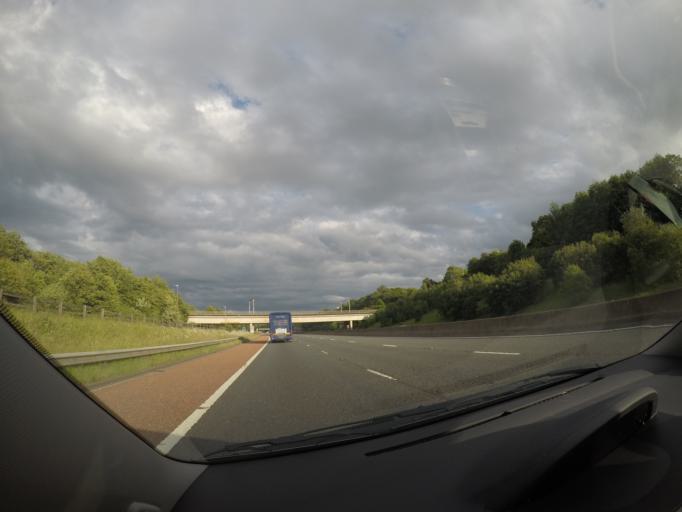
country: GB
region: England
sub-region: Cumbria
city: Penrith
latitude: 54.6570
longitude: -2.7664
